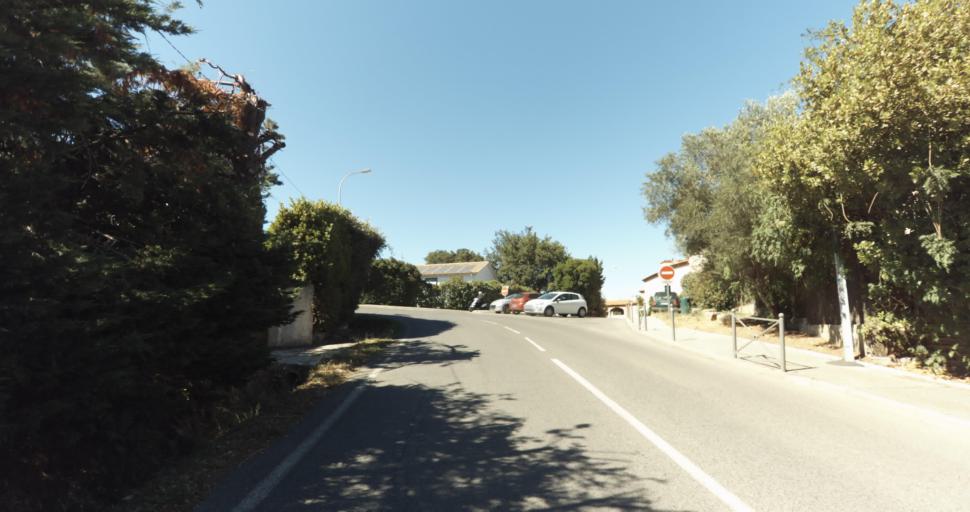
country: FR
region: Provence-Alpes-Cote d'Azur
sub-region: Departement du Var
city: La Croix-Valmer
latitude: 43.2090
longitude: 6.5663
